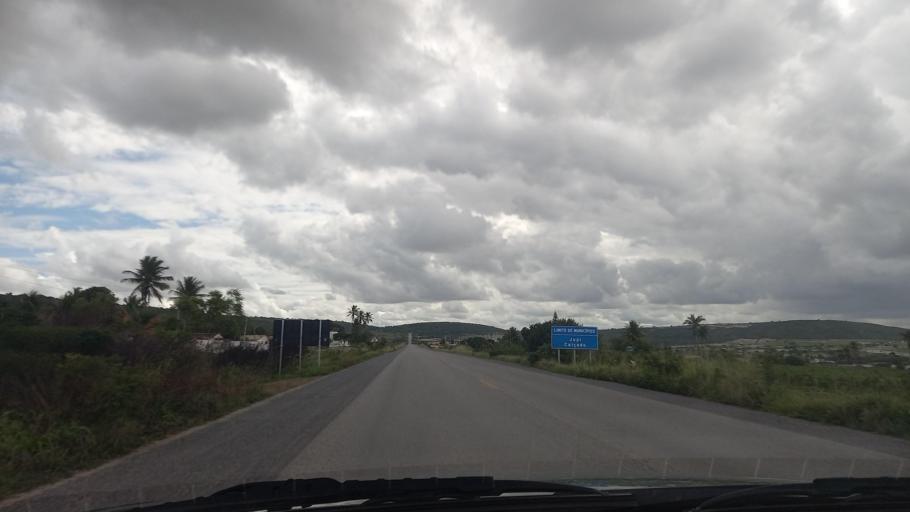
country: BR
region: Pernambuco
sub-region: Lajedo
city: Lajedo
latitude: -8.6681
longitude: -36.3734
